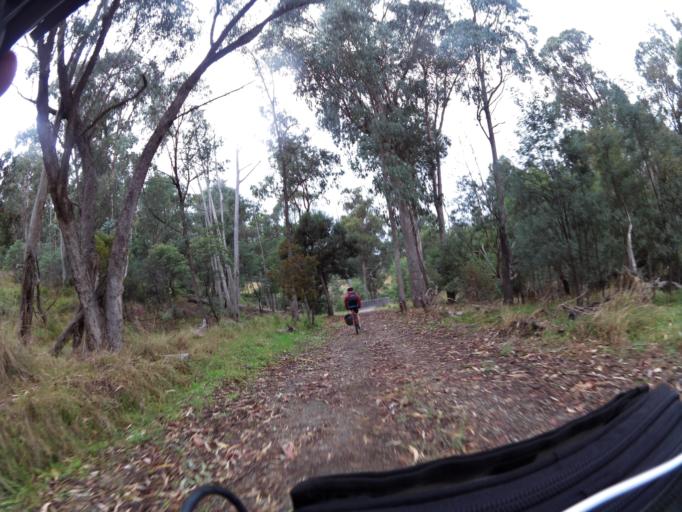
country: AU
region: New South Wales
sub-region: Greater Hume Shire
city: Holbrook
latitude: -36.1681
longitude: 147.4058
